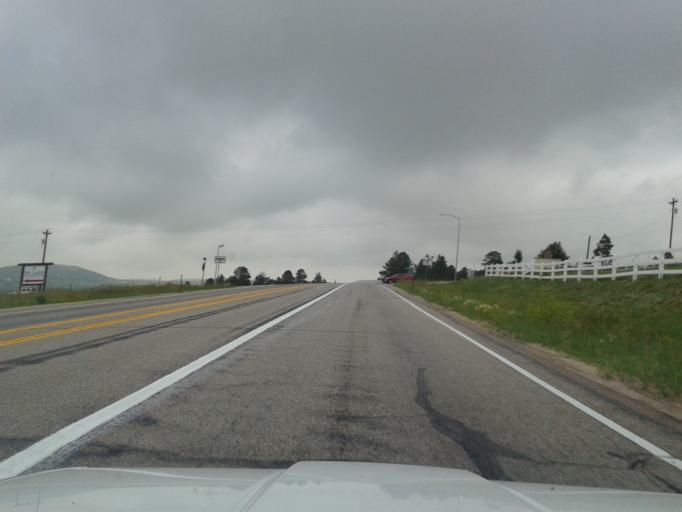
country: US
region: Colorado
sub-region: El Paso County
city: Woodmoor
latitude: 39.1288
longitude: -104.7665
